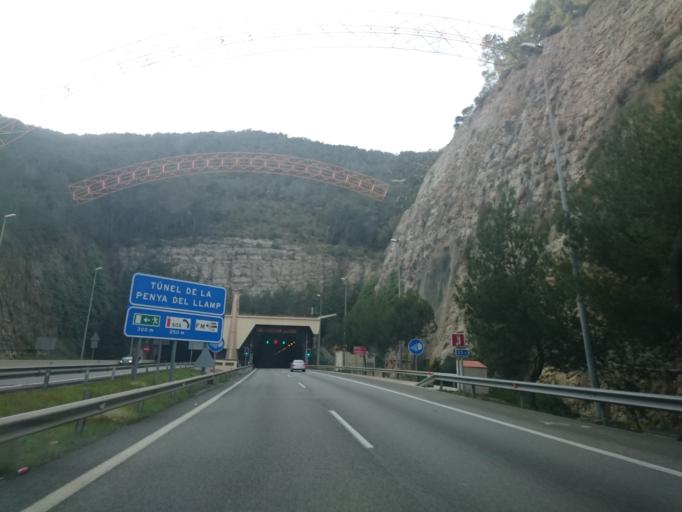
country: ES
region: Catalonia
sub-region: Provincia de Barcelona
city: Sitges
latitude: 41.2461
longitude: 1.8442
